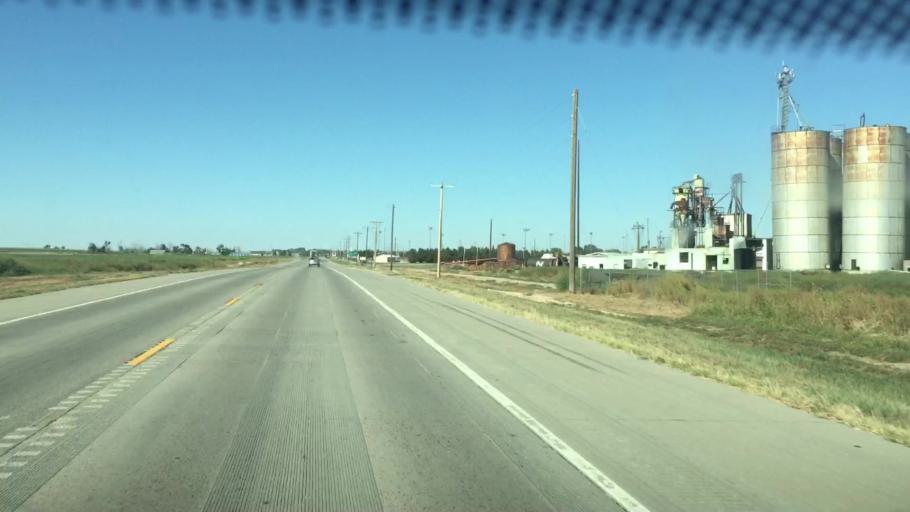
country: US
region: Colorado
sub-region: Prowers County
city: Lamar
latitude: 38.1503
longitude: -102.7233
